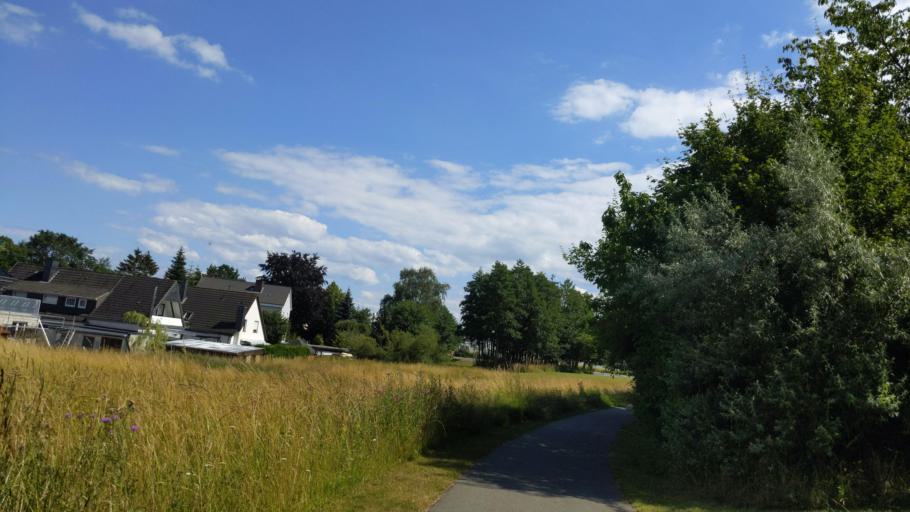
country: DE
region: Schleswig-Holstein
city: Gromitz
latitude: 54.1517
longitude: 10.9474
